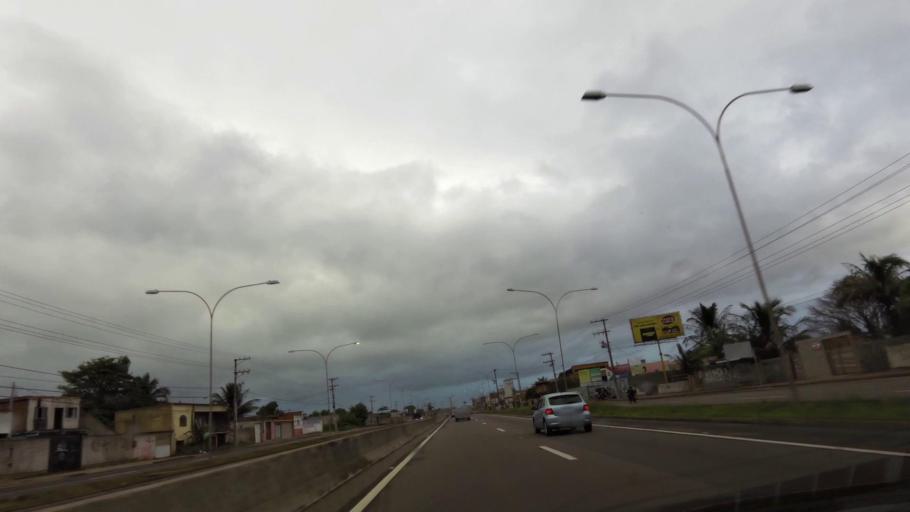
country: BR
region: Espirito Santo
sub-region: Vila Velha
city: Vila Velha
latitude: -20.4431
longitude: -40.3332
